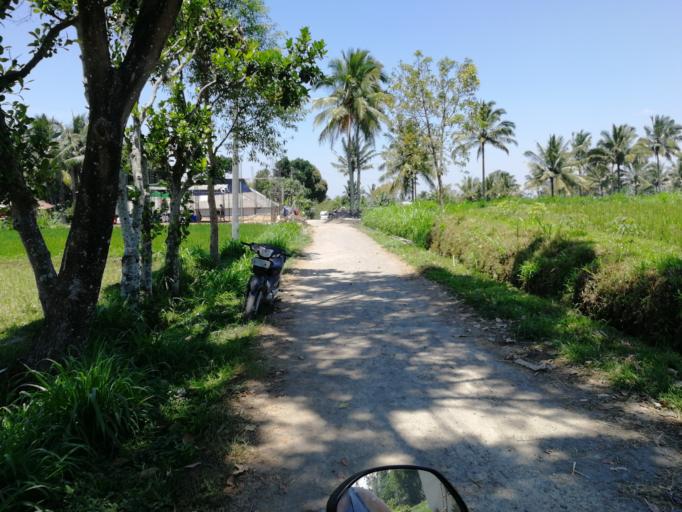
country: ID
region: West Nusa Tenggara
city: Tetebatu
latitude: -8.5430
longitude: 116.4209
